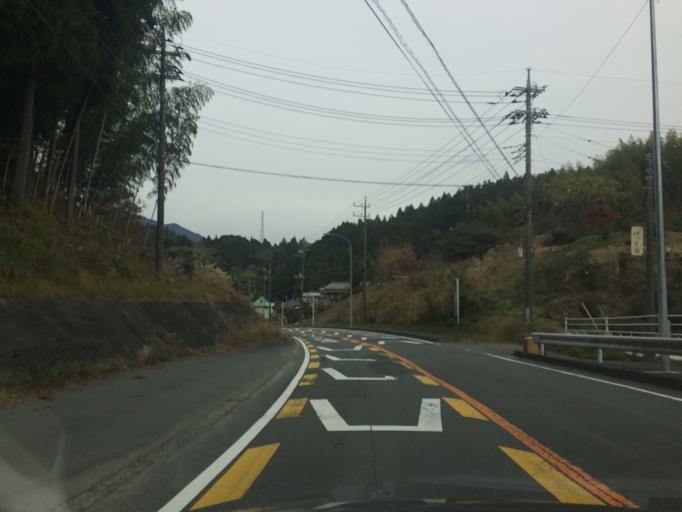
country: JP
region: Shizuoka
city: Fujinomiya
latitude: 35.2763
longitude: 138.4503
